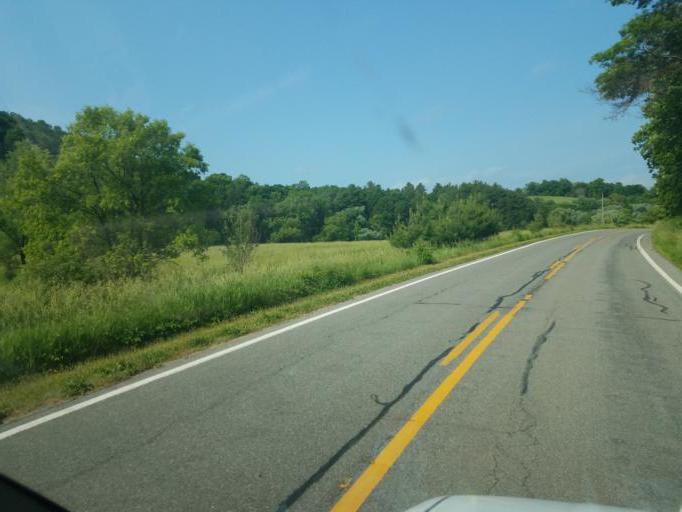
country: US
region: Wisconsin
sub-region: Vernon County
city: Hillsboro
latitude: 43.6837
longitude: -90.5555
